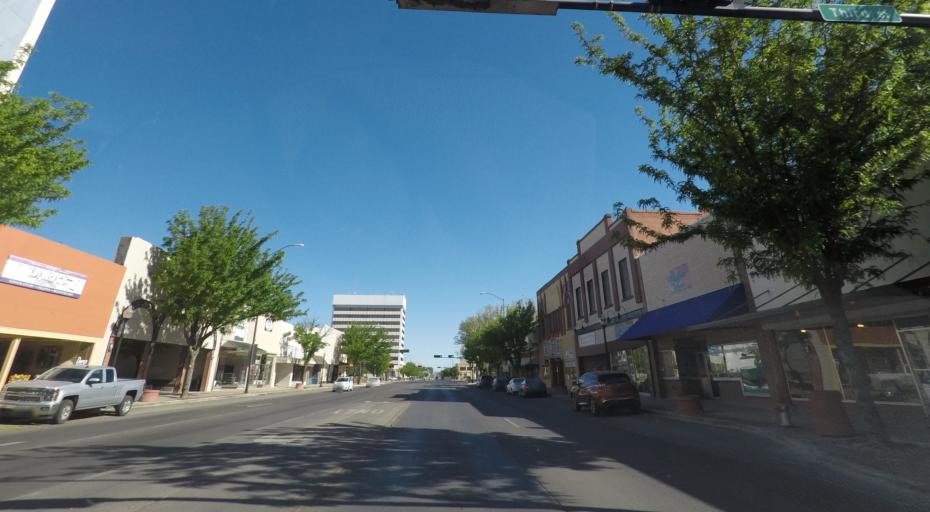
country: US
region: New Mexico
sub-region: Chaves County
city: Roswell
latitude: 33.3954
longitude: -104.5228
